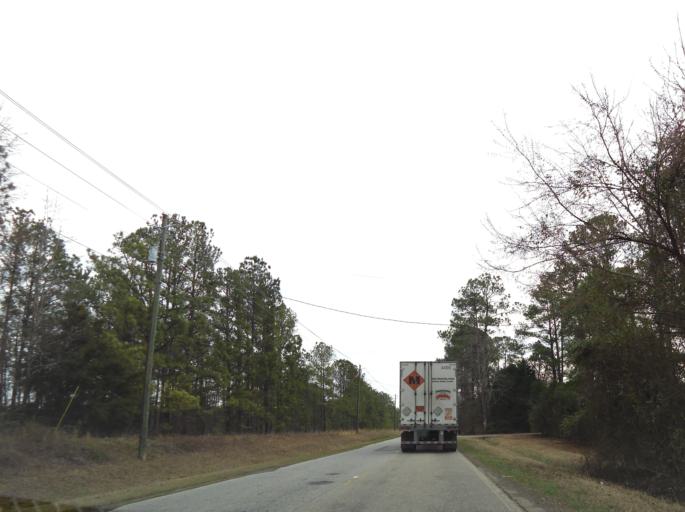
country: US
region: Georgia
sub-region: Houston County
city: Centerville
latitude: 32.6835
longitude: -83.6540
